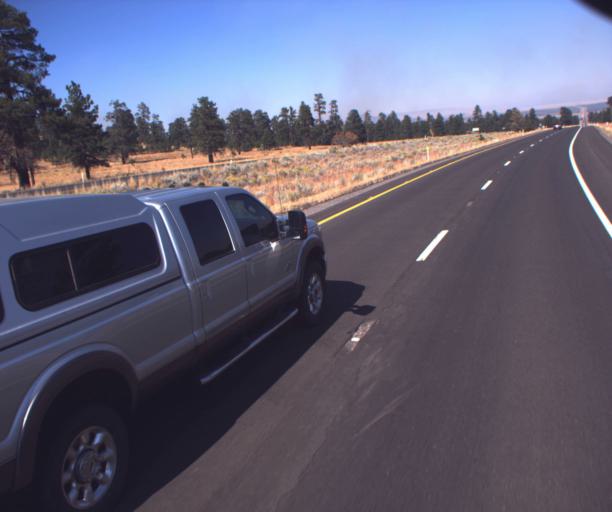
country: US
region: Arizona
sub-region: Coconino County
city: Flagstaff
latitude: 35.3827
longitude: -111.5804
